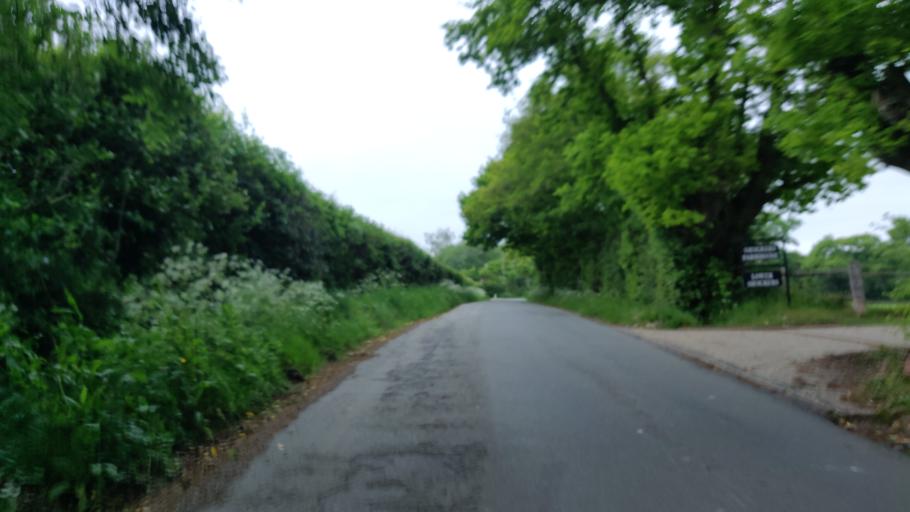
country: GB
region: England
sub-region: West Sussex
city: Southwater
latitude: 51.0083
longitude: -0.3197
